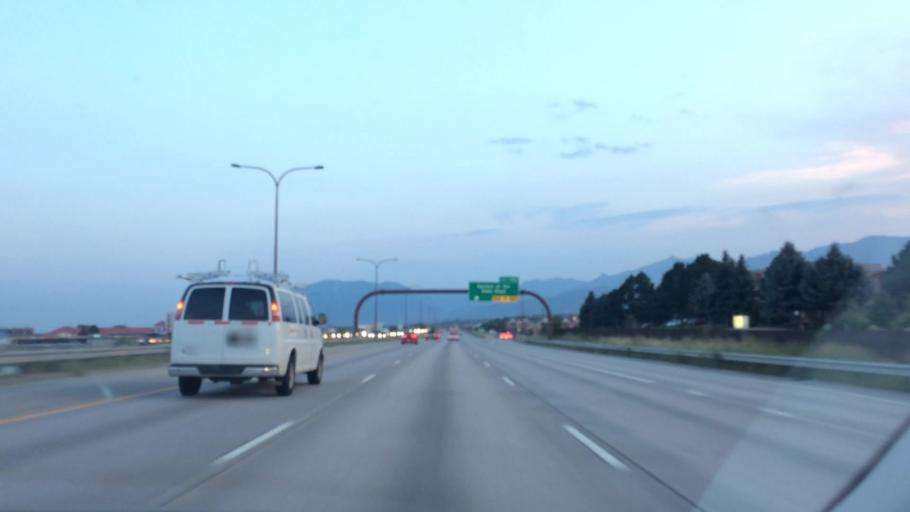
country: US
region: Colorado
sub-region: El Paso County
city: Colorado Springs
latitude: 38.9023
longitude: -104.8287
